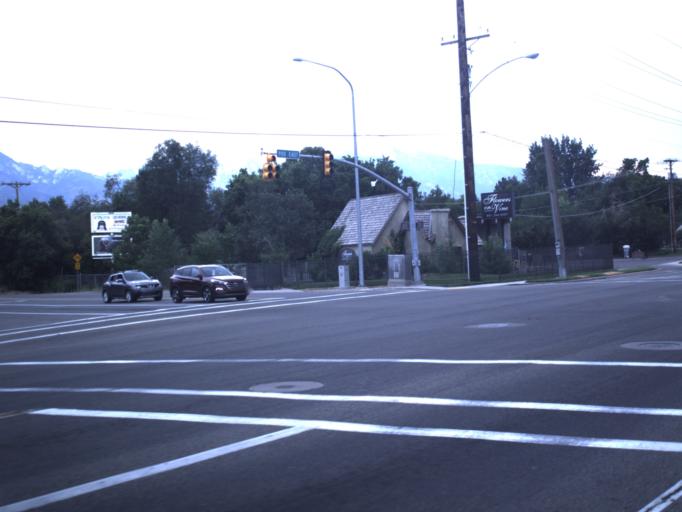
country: US
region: Utah
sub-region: Salt Lake County
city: Murray
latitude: 40.6423
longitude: -111.8661
